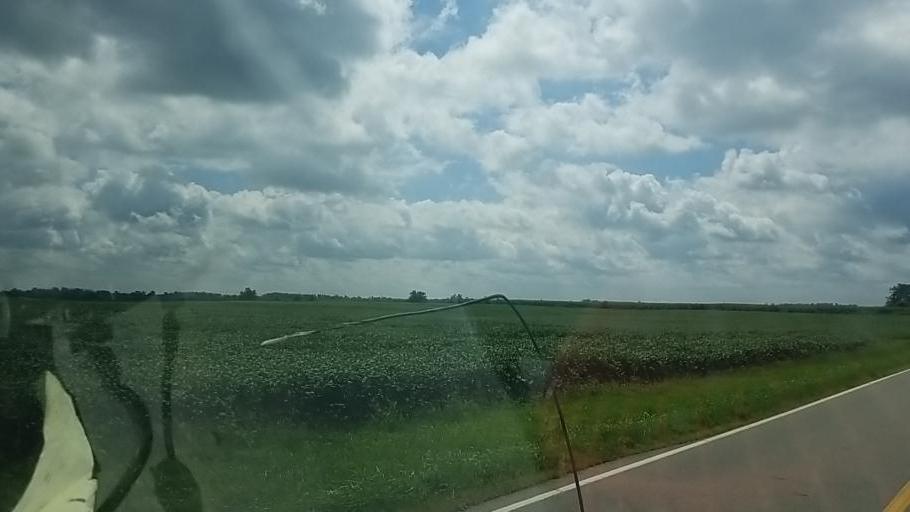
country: US
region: Ohio
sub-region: Fayette County
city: Jeffersonville
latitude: 39.6817
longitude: -83.5039
